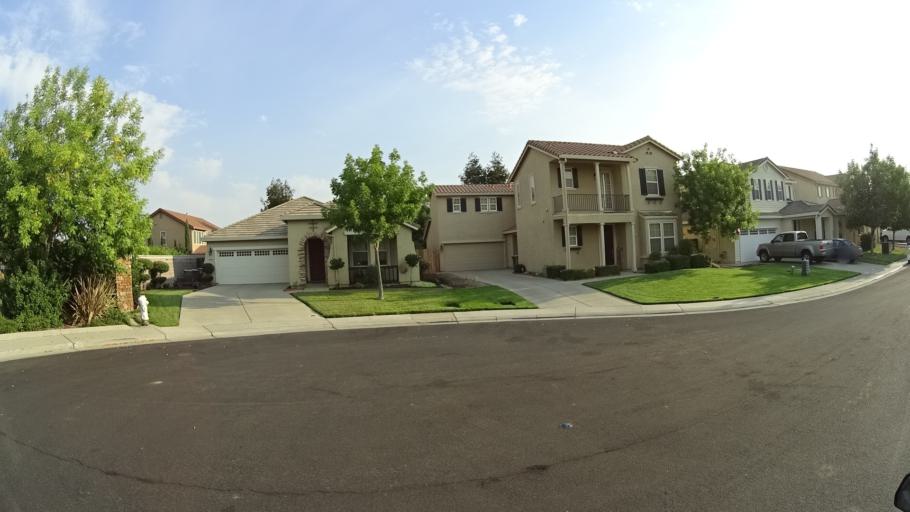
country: US
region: California
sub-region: Sacramento County
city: Laguna
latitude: 38.3845
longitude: -121.4193
